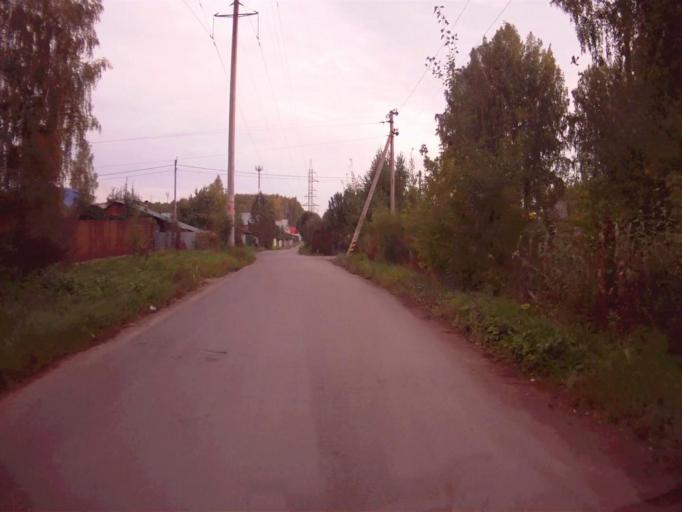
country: RU
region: Chelyabinsk
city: Sargazy
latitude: 55.1368
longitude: 61.2488
